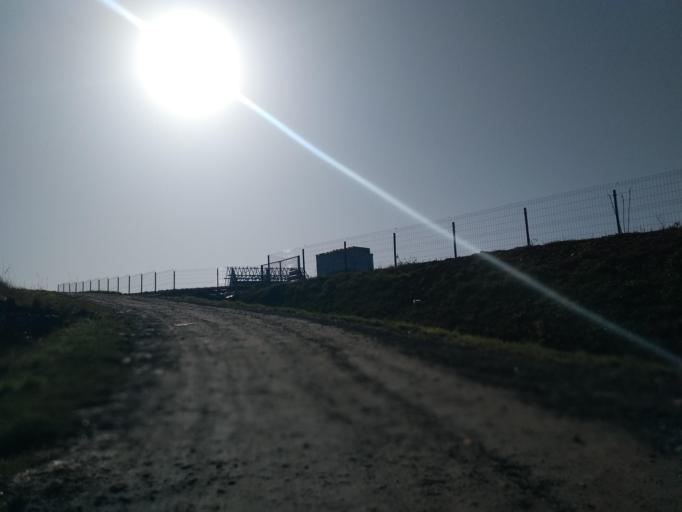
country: PL
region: Subcarpathian Voivodeship
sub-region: Powiat rzeszowski
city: Blazowa
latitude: 49.8691
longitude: 22.1216
